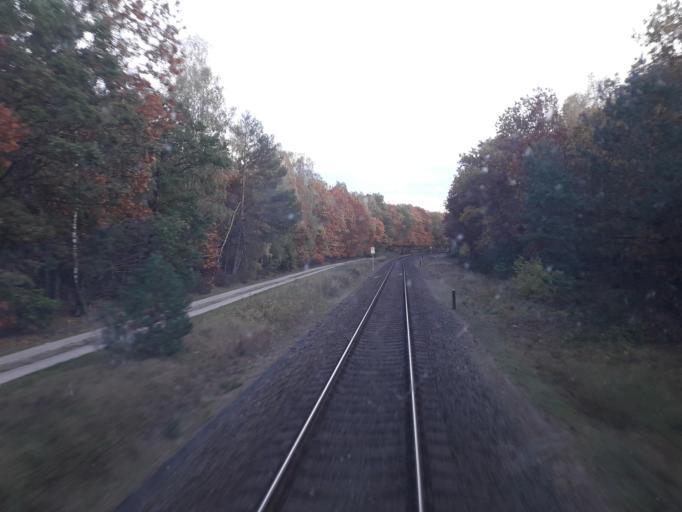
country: DE
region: Brandenburg
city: Walsleben
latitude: 52.9660
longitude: 12.6554
